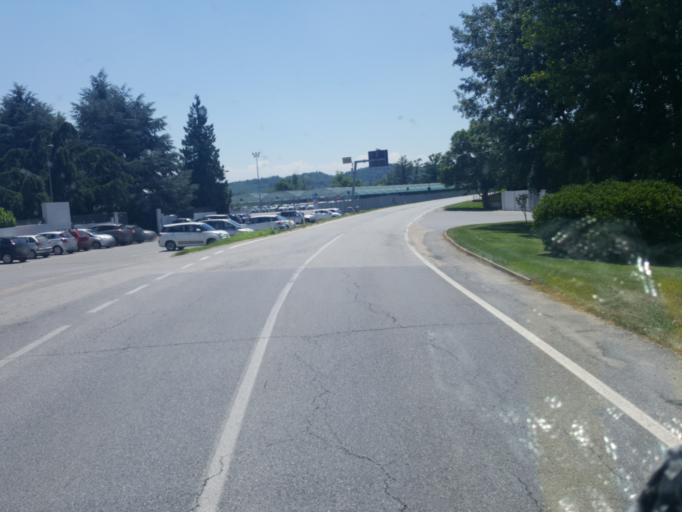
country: IT
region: Piedmont
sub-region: Provincia di Cuneo
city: Cherasco
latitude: 44.6500
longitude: 7.8700
